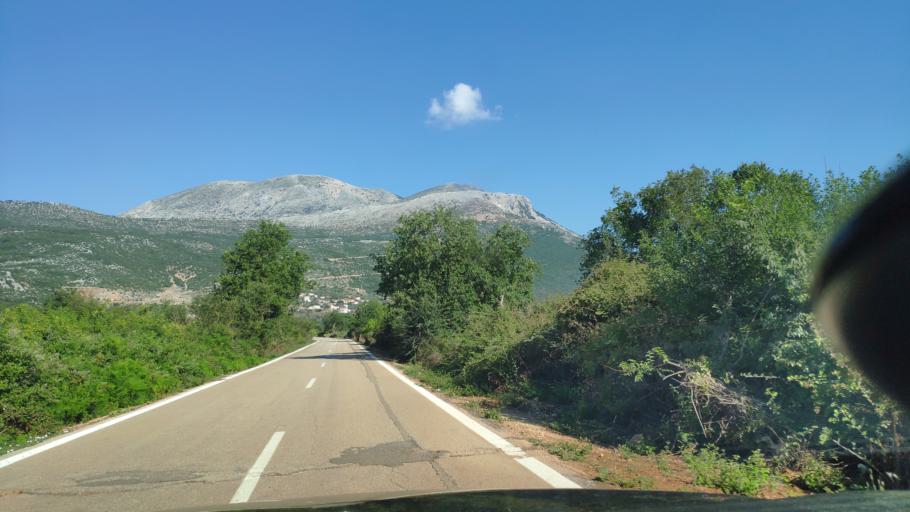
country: GR
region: West Greece
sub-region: Nomos Aitolias kai Akarnanias
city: Archontochorion
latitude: 38.7000
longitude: 21.0953
